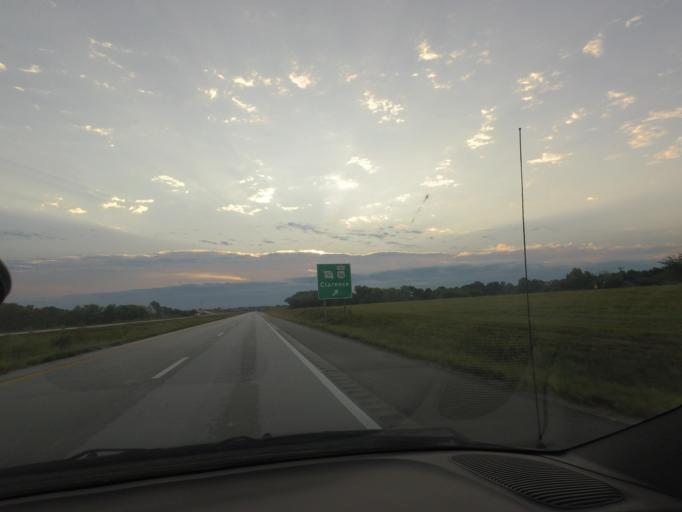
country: US
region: Missouri
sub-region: Macon County
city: Macon
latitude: 39.7510
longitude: -92.2669
